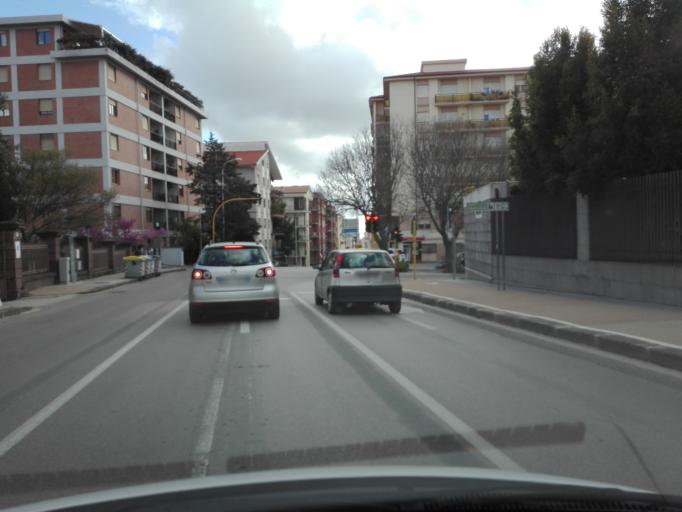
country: IT
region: Sardinia
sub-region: Provincia di Sassari
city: Sassari
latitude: 40.7171
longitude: 8.5692
